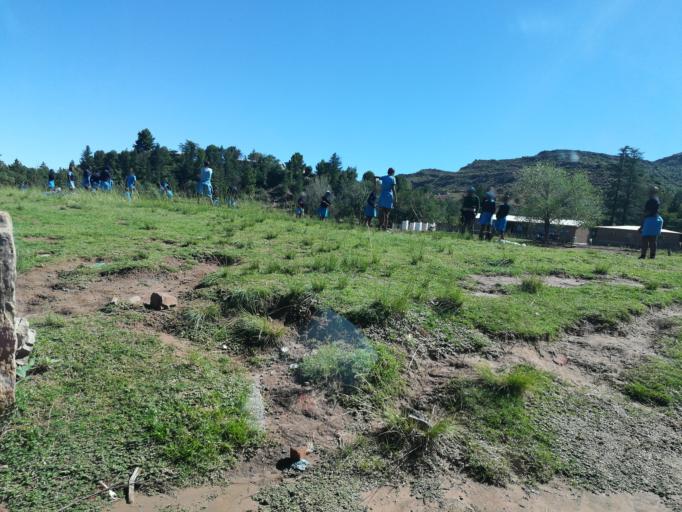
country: LS
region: Quthing
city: Quthing
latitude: -30.3435
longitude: 27.5433
